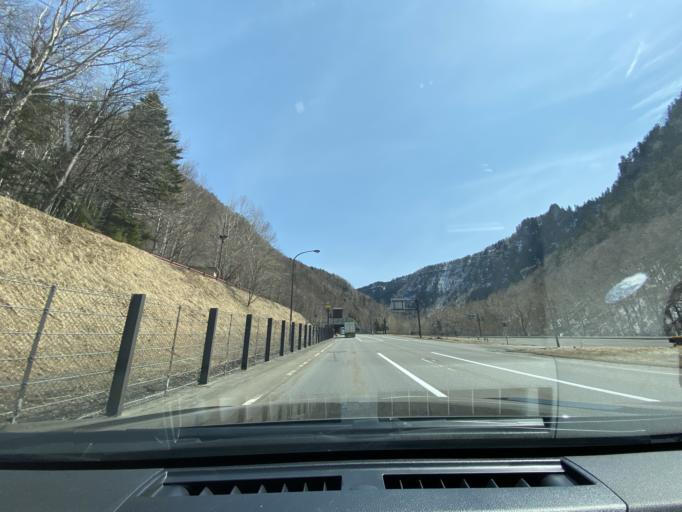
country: JP
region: Hokkaido
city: Kamikawa
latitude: 43.7234
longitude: 142.9728
